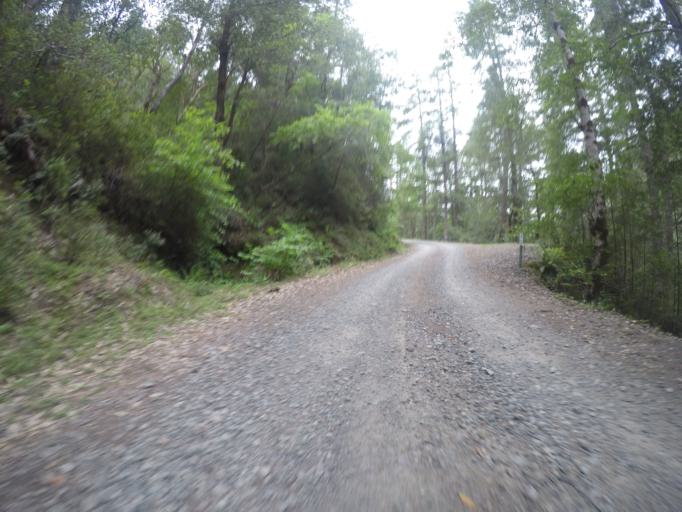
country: US
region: California
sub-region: Del Norte County
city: Bertsch-Oceanview
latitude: 41.7415
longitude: -123.8790
